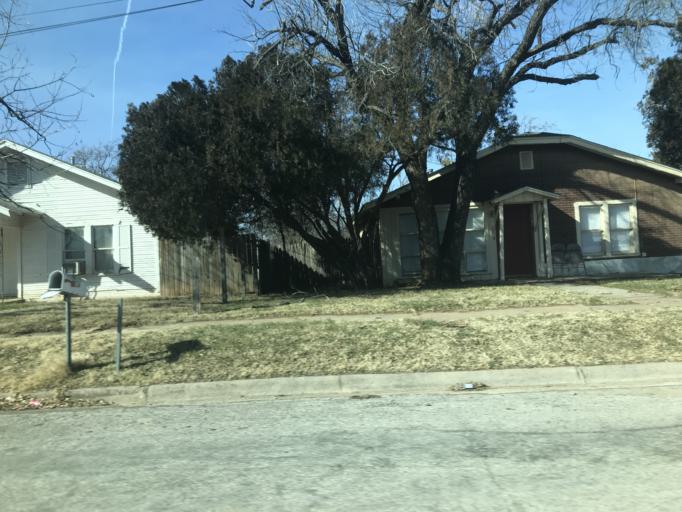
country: US
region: Texas
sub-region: Taylor County
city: Abilene
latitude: 32.4728
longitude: -99.7417
